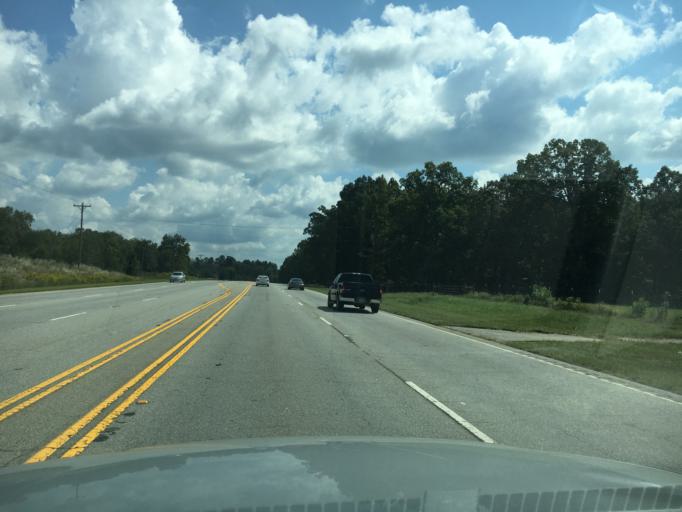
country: US
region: South Carolina
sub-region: Anderson County
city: Williamston
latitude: 34.6065
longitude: -82.3661
